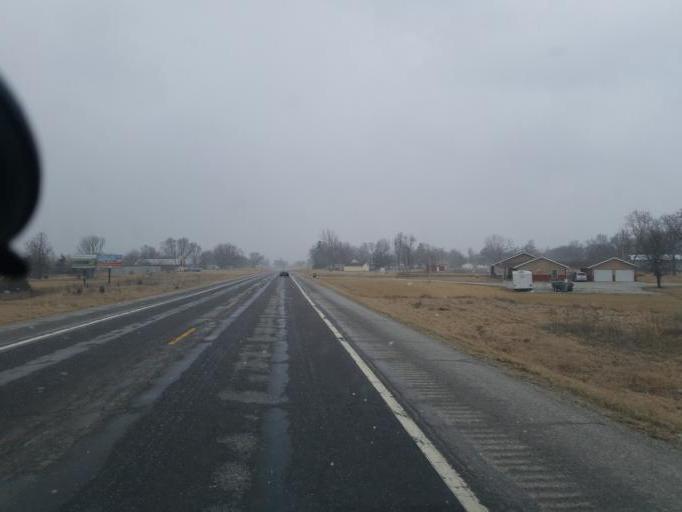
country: US
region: Missouri
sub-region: Schuyler County
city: Lancaster
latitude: 40.4150
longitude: -92.5646
